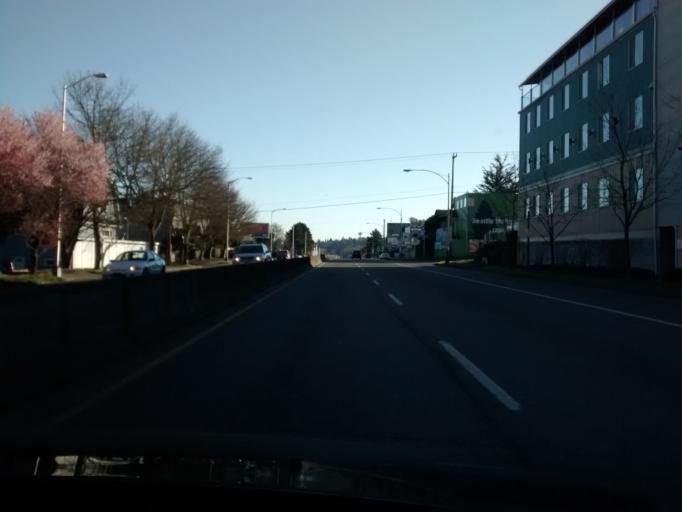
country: US
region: Washington
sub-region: King County
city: Seattle
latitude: 47.6643
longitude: -122.3473
